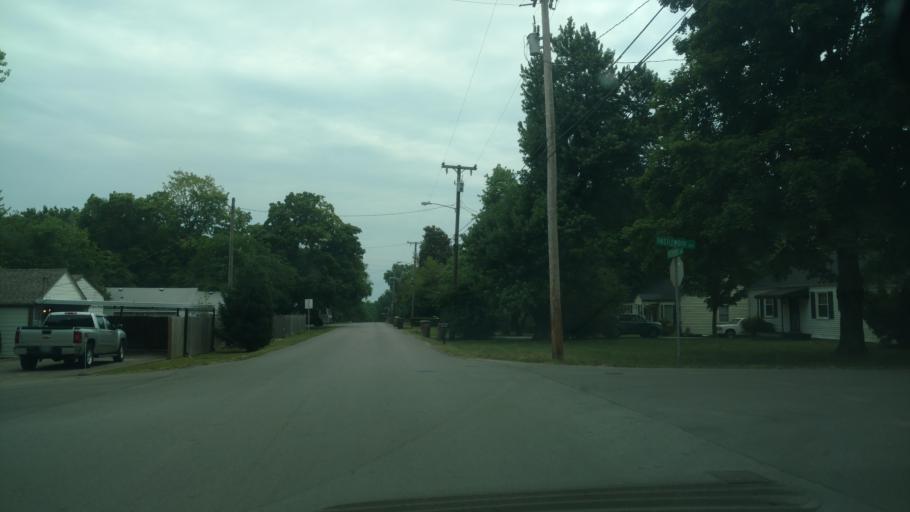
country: US
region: Tennessee
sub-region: Davidson County
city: Nashville
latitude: 36.2014
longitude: -86.7187
